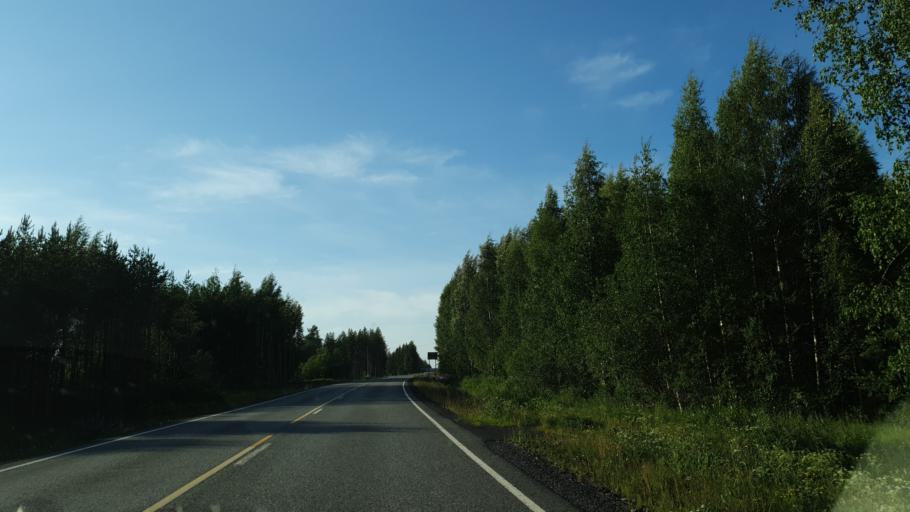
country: FI
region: Kainuu
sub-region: Kehys-Kainuu
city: Kuhmo
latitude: 64.0792
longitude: 29.4867
